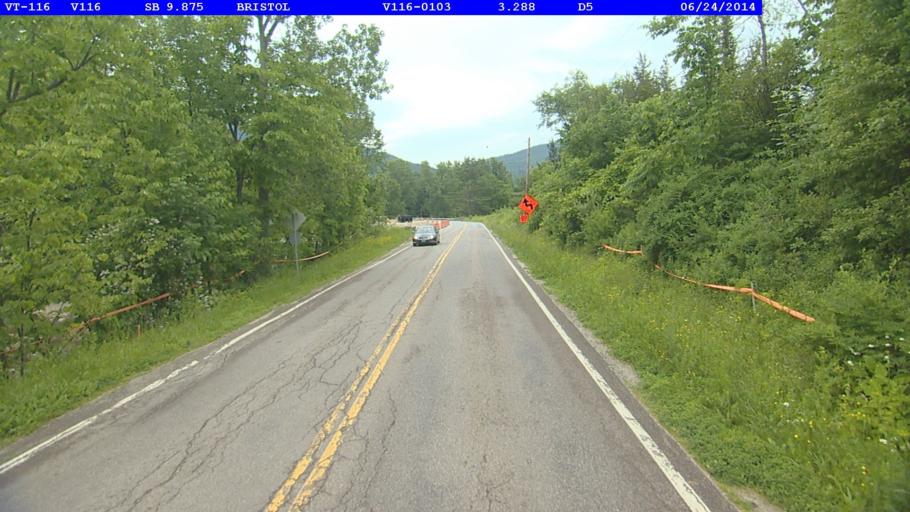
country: US
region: Vermont
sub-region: Addison County
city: Bristol
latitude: 44.0983
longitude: -73.0954
